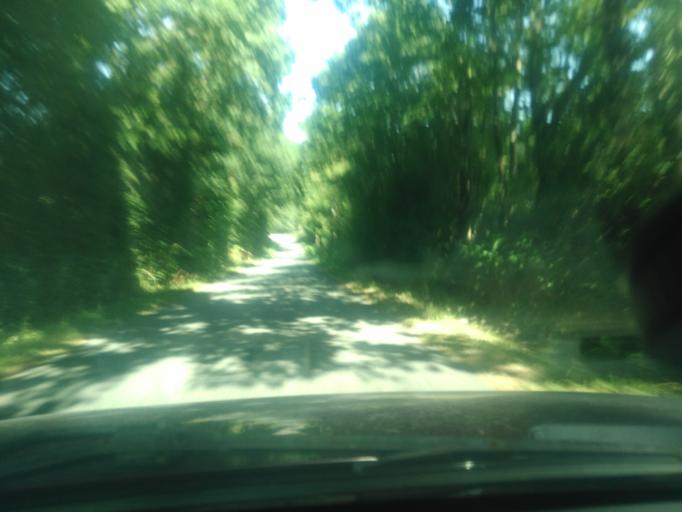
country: FR
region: Pays de la Loire
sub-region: Departement de la Vendee
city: La Ferriere
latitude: 46.7144
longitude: -1.3388
